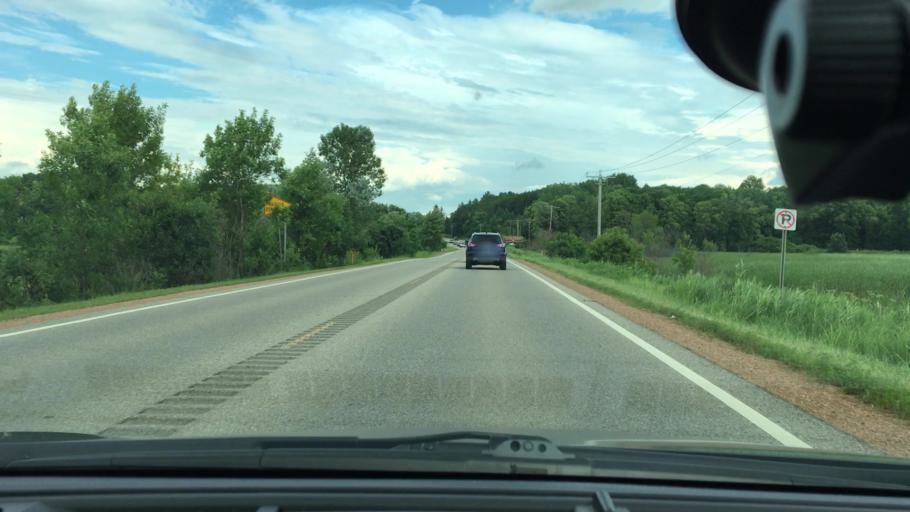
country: US
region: Minnesota
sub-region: Hennepin County
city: Shorewood
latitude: 44.8650
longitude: -93.6133
